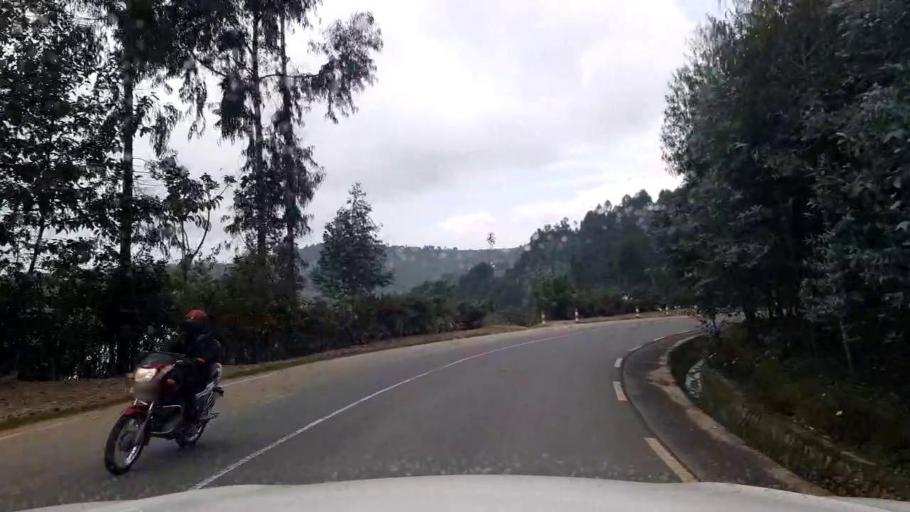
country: RW
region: Northern Province
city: Musanze
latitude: -1.6632
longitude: 29.5121
